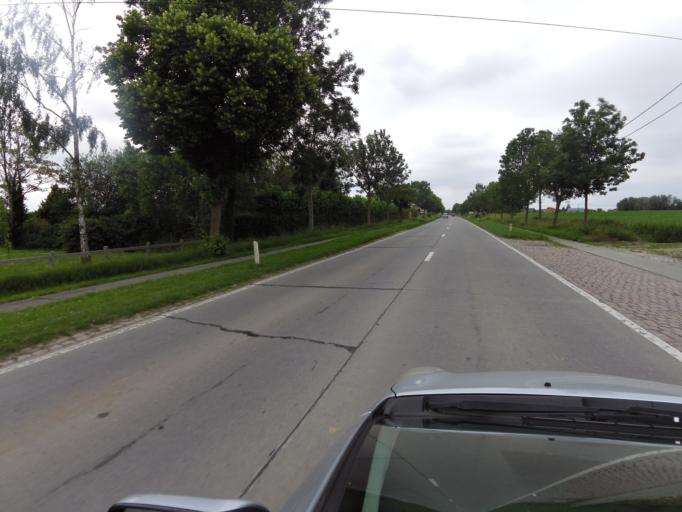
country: BE
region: Flanders
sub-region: Provincie West-Vlaanderen
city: Diksmuide
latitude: 50.9434
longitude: 2.8612
